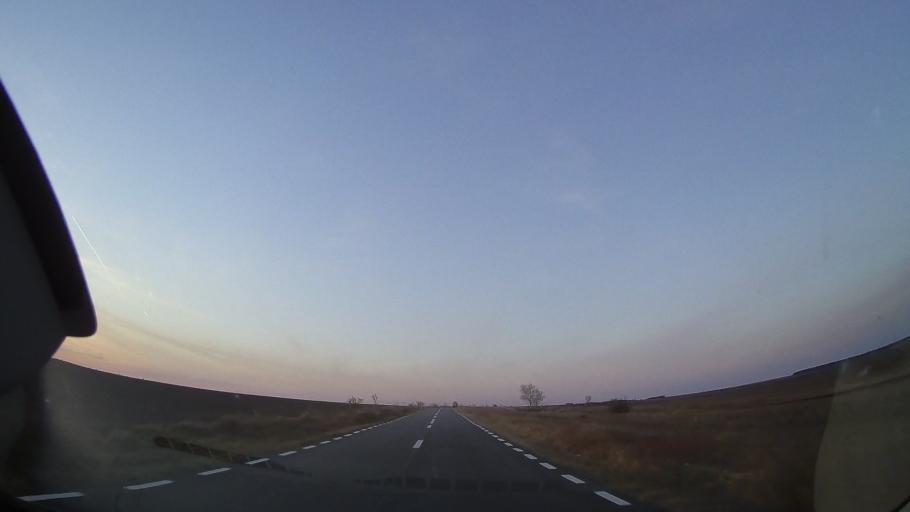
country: RO
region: Constanta
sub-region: Comuna Cobadin
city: Cobadin
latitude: 44.0253
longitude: 28.2651
